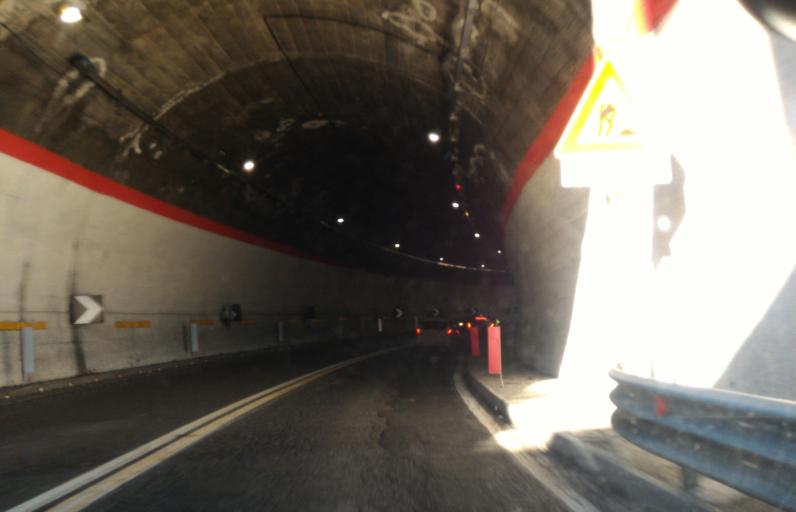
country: IT
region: Calabria
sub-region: Provincia di Cosenza
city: Celico
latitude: 39.3079
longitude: 16.3406
